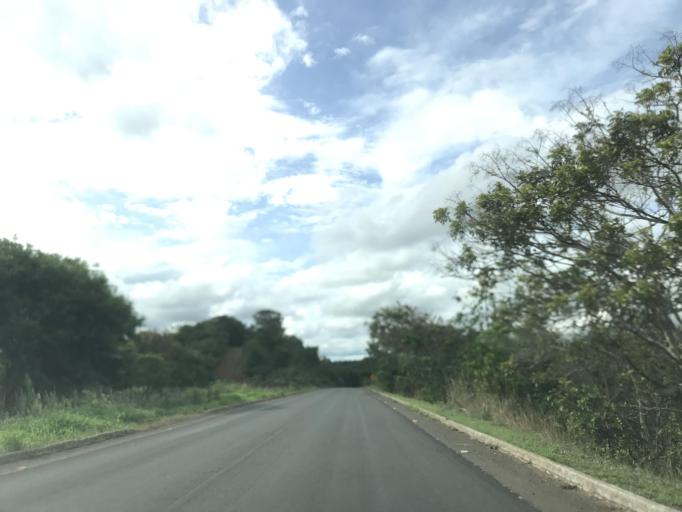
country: BR
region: Goias
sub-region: Bela Vista De Goias
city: Bela Vista de Goias
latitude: -17.0135
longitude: -48.6606
